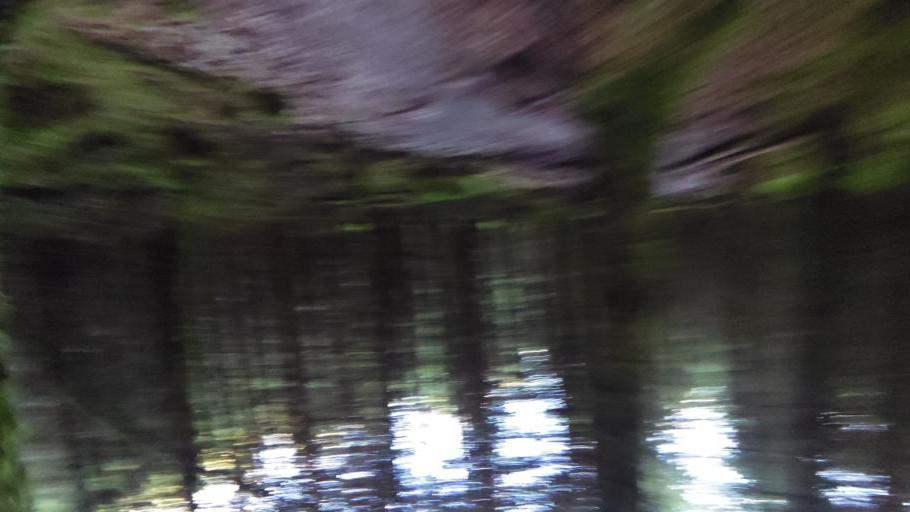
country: GB
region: England
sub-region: Lancashire
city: Clitheroe
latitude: 54.0040
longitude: -2.4010
